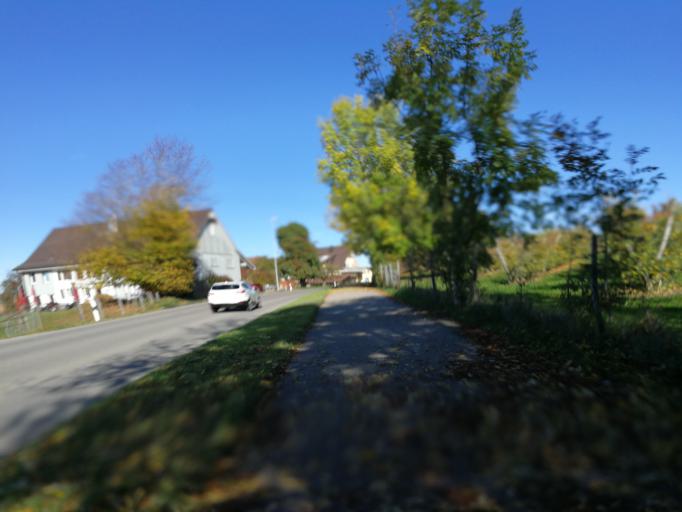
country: CH
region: Zurich
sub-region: Bezirk Meilen
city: Oetwil am See
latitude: 47.2694
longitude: 8.7393
